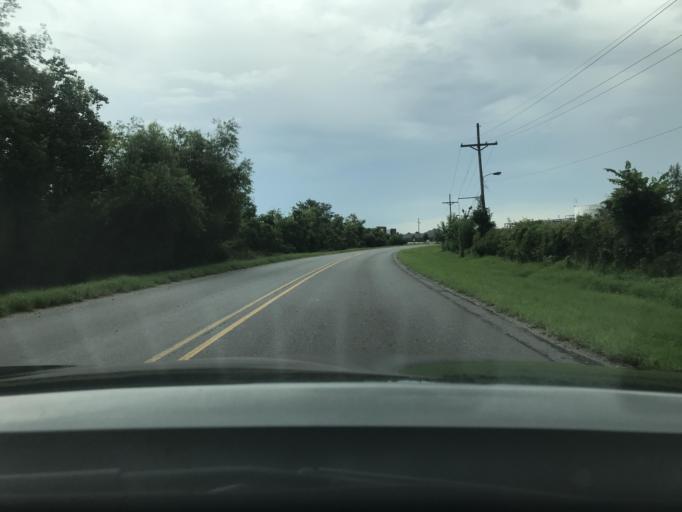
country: US
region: Louisiana
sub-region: Calcasieu Parish
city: Westlake
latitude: 30.2346
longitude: -93.2535
